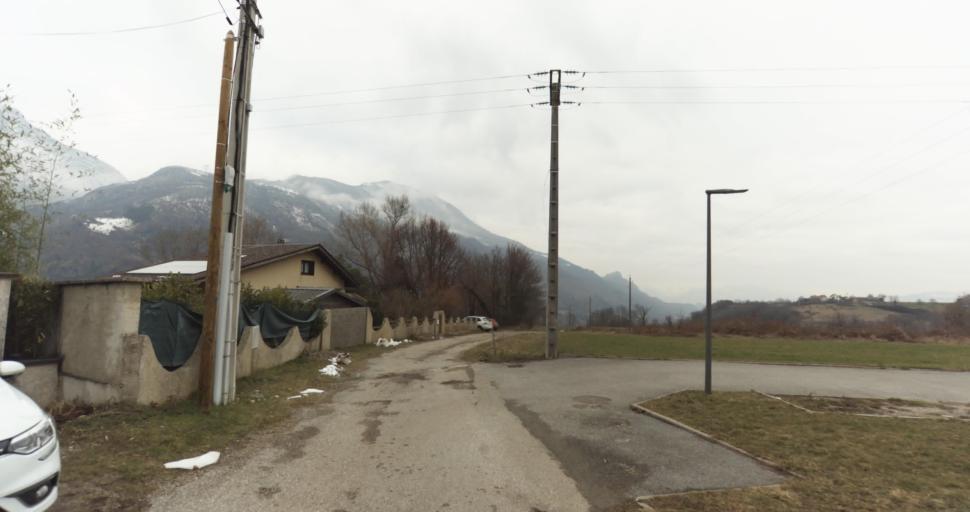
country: FR
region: Rhone-Alpes
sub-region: Departement de l'Isere
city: Le Gua
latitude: 45.0216
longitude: 5.6543
